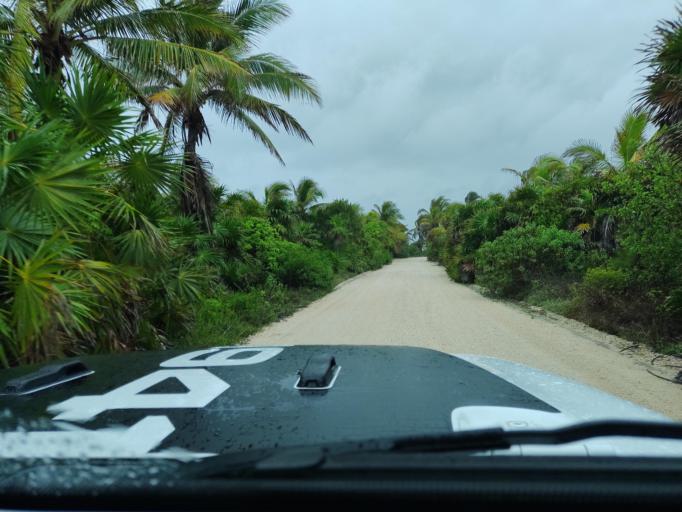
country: MX
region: Quintana Roo
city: Tulum
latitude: 19.9868
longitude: -87.4648
